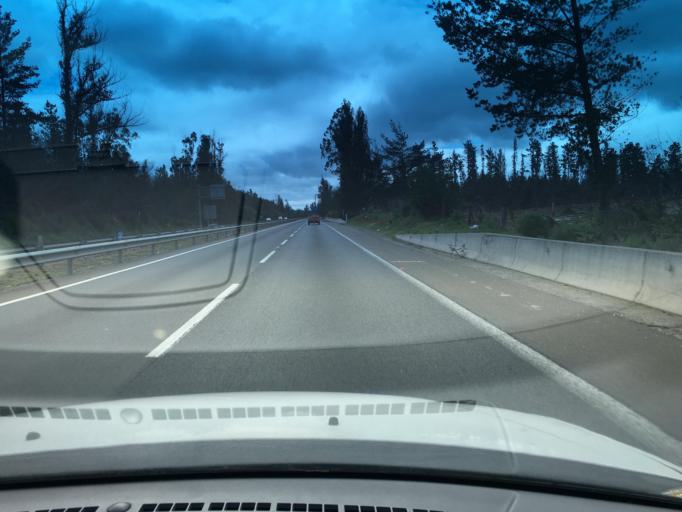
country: CL
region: Valparaiso
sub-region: Provincia de Valparaiso
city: Vina del Mar
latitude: -33.1579
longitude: -71.5484
